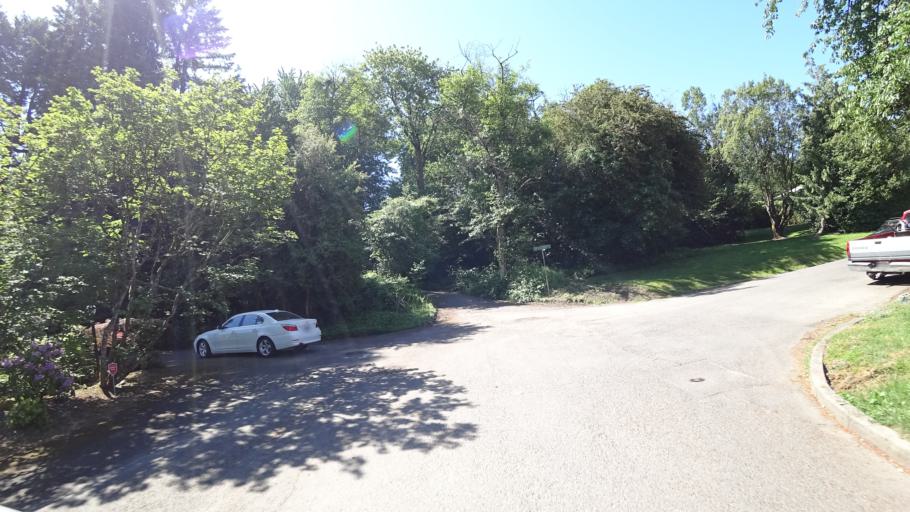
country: US
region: Oregon
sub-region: Washington County
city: Raleigh Hills
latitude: 45.4860
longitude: -122.7310
